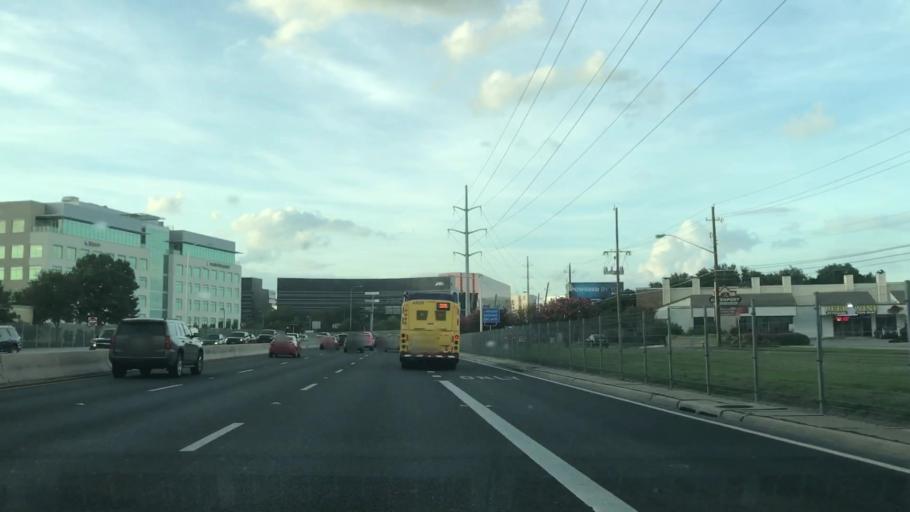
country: US
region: Texas
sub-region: Dallas County
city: Addison
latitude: 32.9445
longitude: -96.8227
